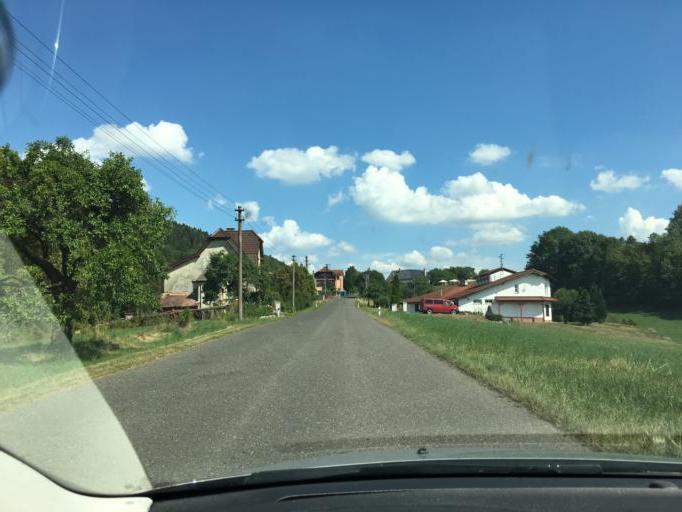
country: CZ
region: Liberecky
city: Mala Skala
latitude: 50.6528
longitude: 15.1513
